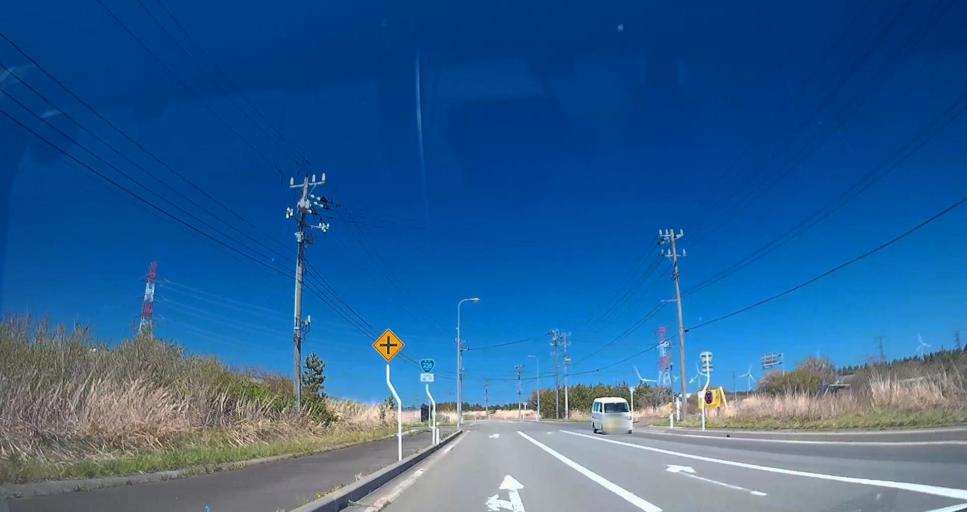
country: JP
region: Hokkaido
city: Hakodate
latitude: 41.5085
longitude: 140.9180
